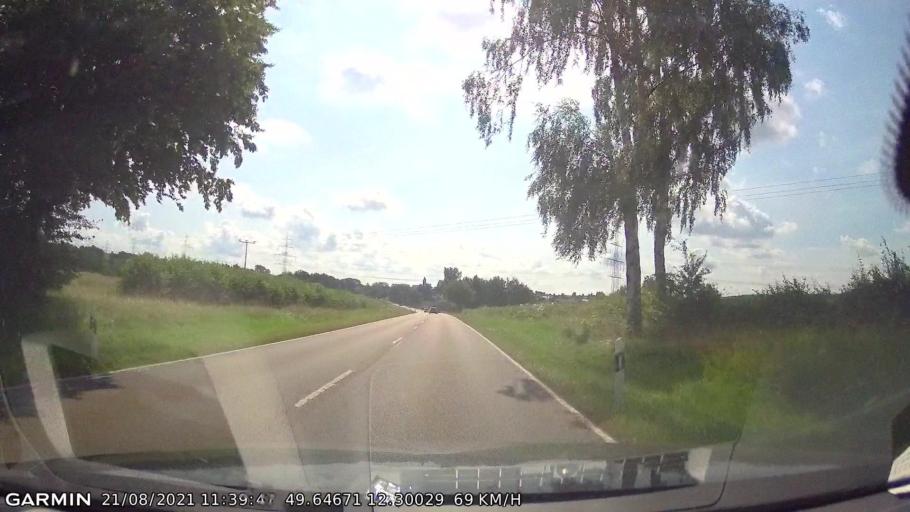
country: DE
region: Bavaria
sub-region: Upper Palatinate
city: Waldthurn
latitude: 49.6466
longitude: 12.3004
